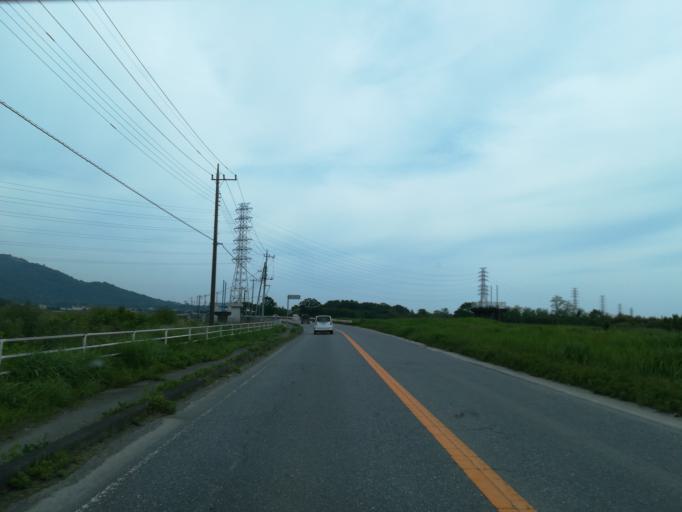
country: JP
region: Ibaraki
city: Tsukuba
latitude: 36.1449
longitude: 140.1044
